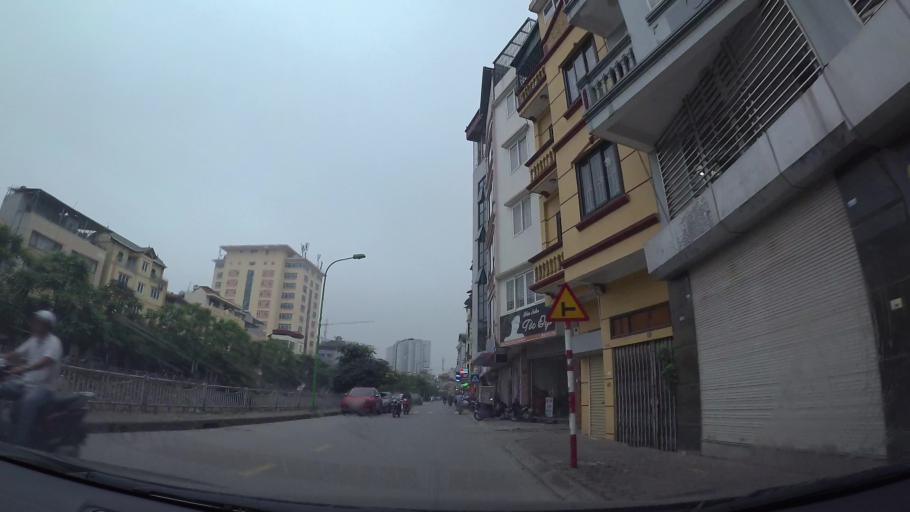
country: VN
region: Ha Noi
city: Hai BaTrung
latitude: 20.9899
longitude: 105.8370
